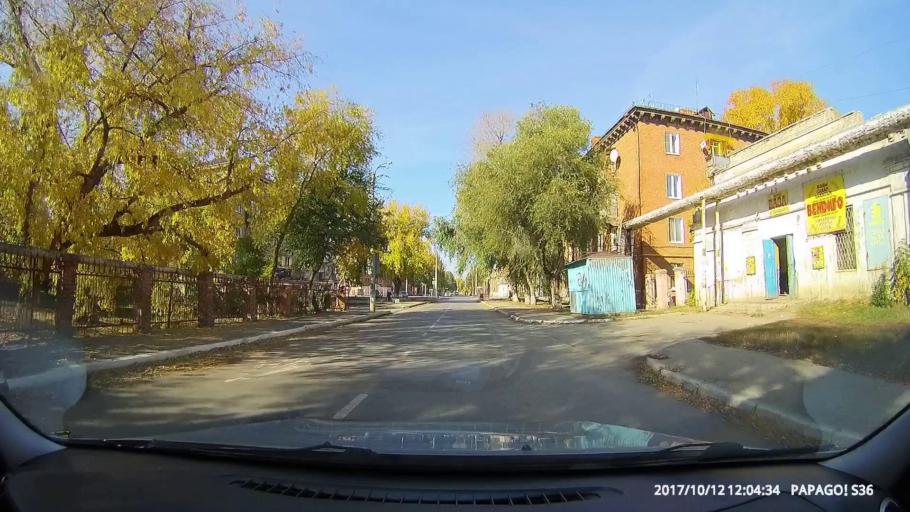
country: RU
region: Samara
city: Chapayevsk
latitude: 52.9785
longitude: 49.7149
